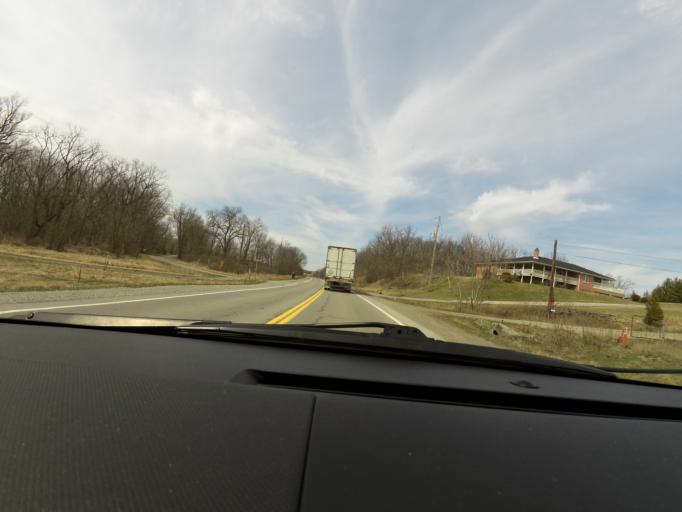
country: CA
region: Ontario
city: Ancaster
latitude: 43.0049
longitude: -79.8688
